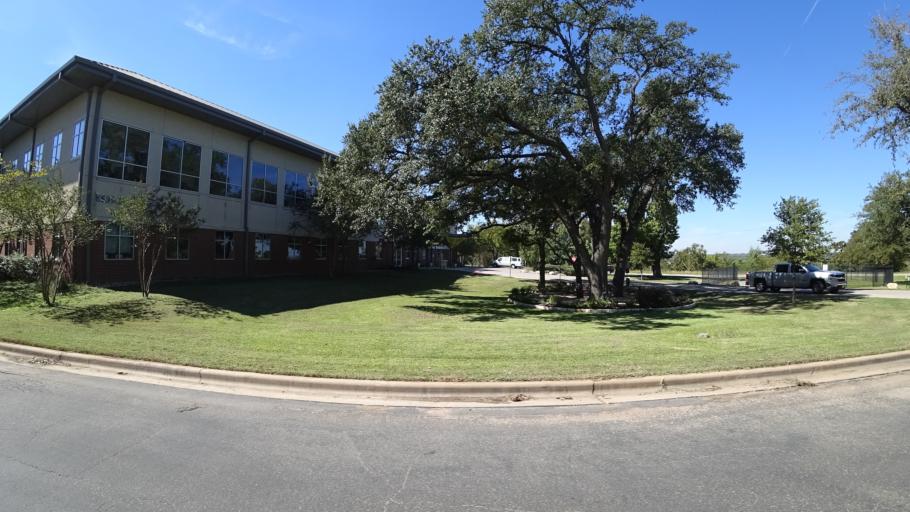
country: US
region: Texas
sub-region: Travis County
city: Hornsby Bend
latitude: 30.2737
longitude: -97.6384
